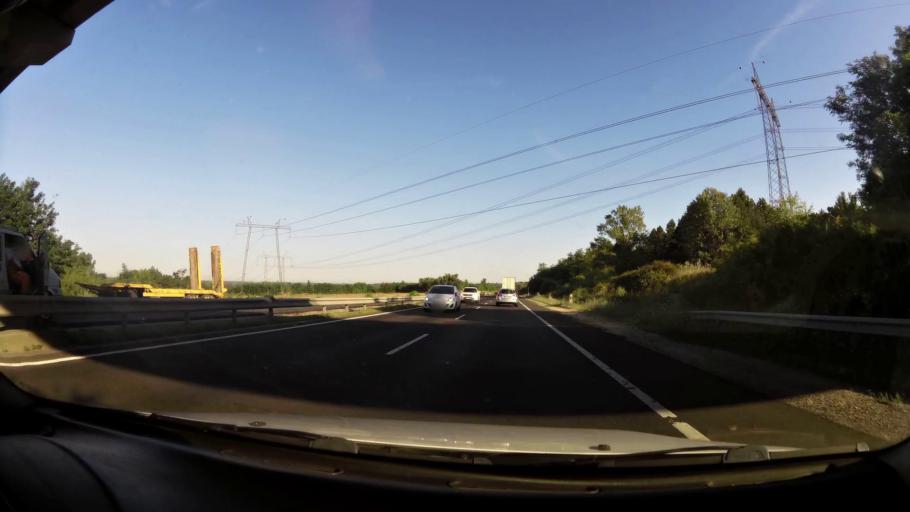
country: HU
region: Pest
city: Cegledbercel
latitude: 47.2347
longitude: 19.6674
